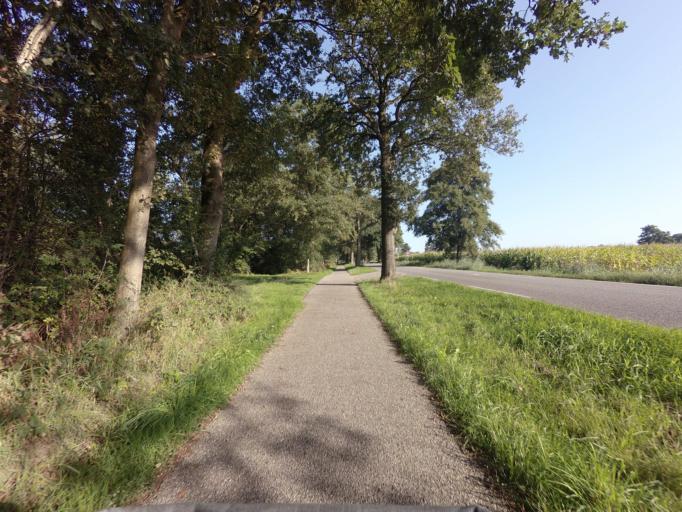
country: NL
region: Overijssel
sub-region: Gemeente Raalte
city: Raalte
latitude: 52.3230
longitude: 6.2838
